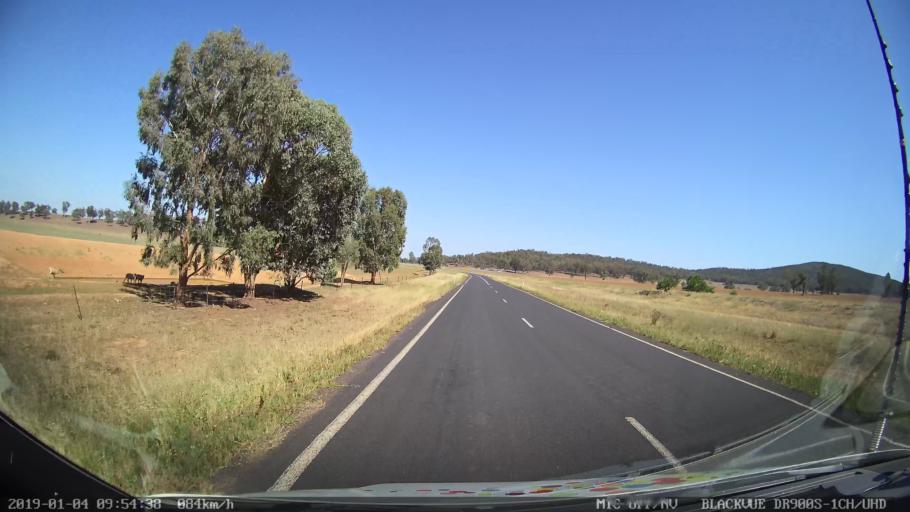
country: AU
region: New South Wales
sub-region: Cabonne
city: Canowindra
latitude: -33.5396
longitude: 148.4127
